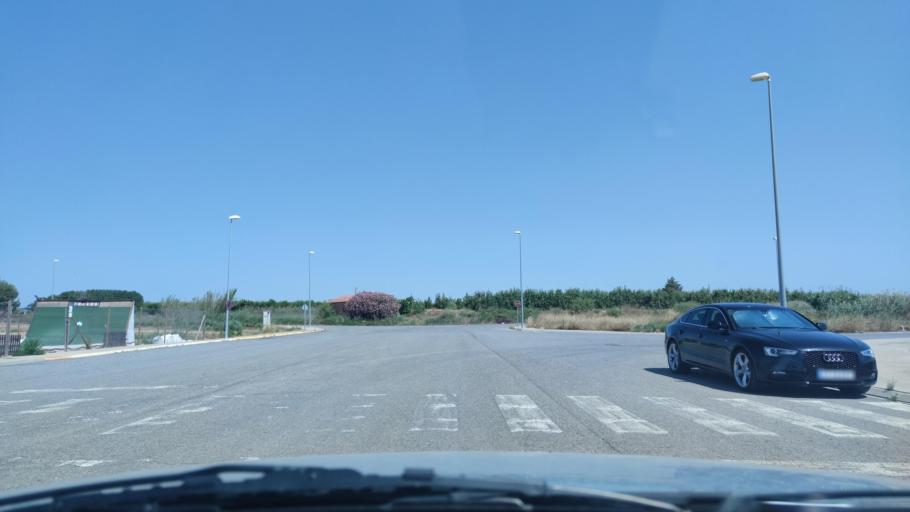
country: ES
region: Catalonia
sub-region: Provincia de Lleida
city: Torrefarrera
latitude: 41.6680
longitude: 0.5966
